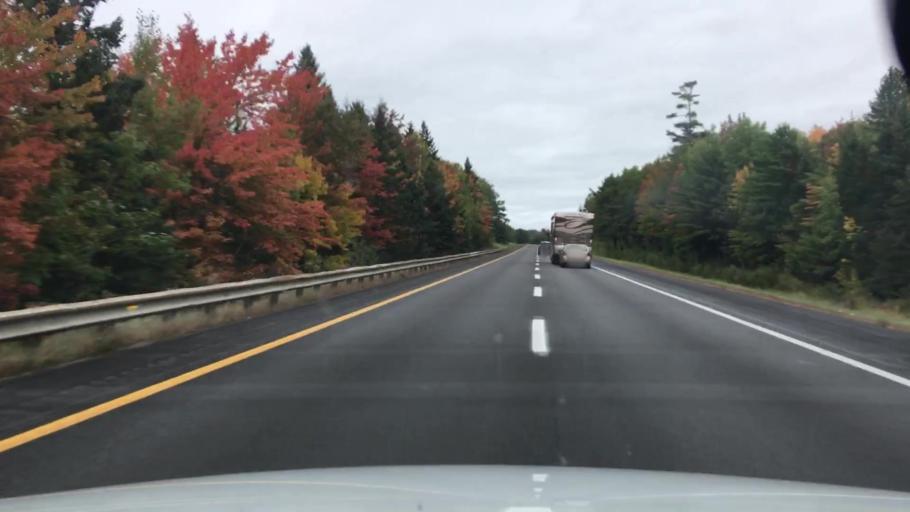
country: US
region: Maine
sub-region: Penobscot County
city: Veazie
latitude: 44.8532
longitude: -68.7244
